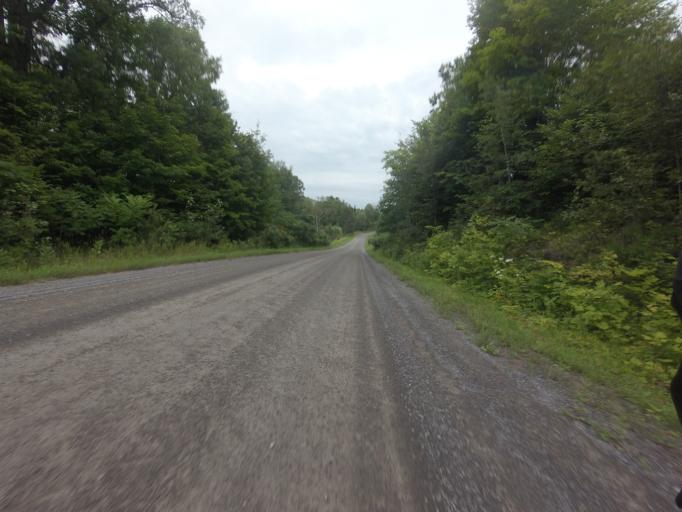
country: CA
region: Ontario
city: Carleton Place
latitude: 45.1649
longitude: -76.2738
